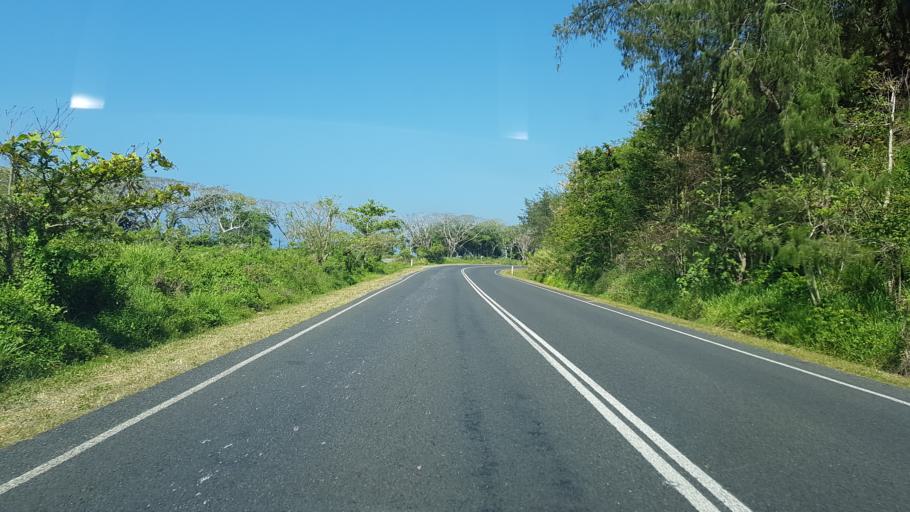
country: FJ
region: Western
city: Nadi
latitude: -18.1840
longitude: 177.6010
